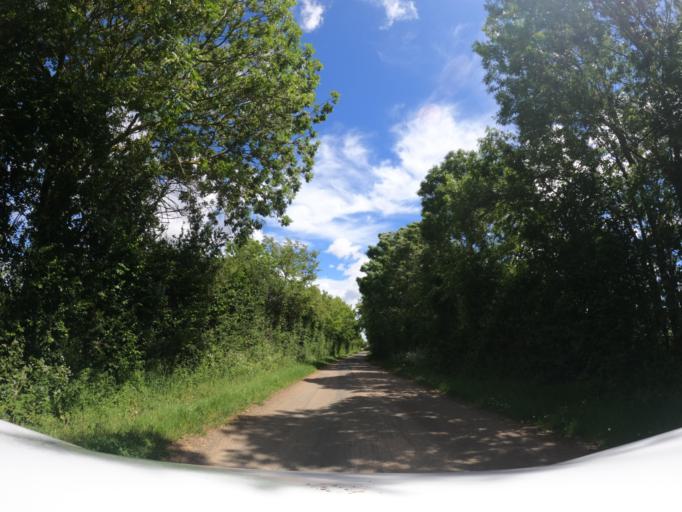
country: FR
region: Pays de la Loire
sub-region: Departement de la Vendee
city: Le Champ-Saint-Pere
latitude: 46.4775
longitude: -1.3170
